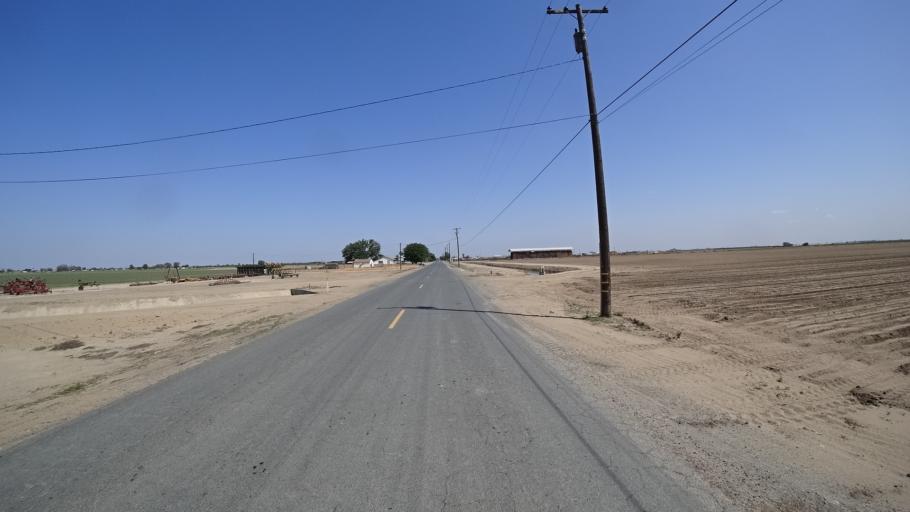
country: US
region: California
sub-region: Kings County
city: Home Garden
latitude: 36.2736
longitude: -119.6190
